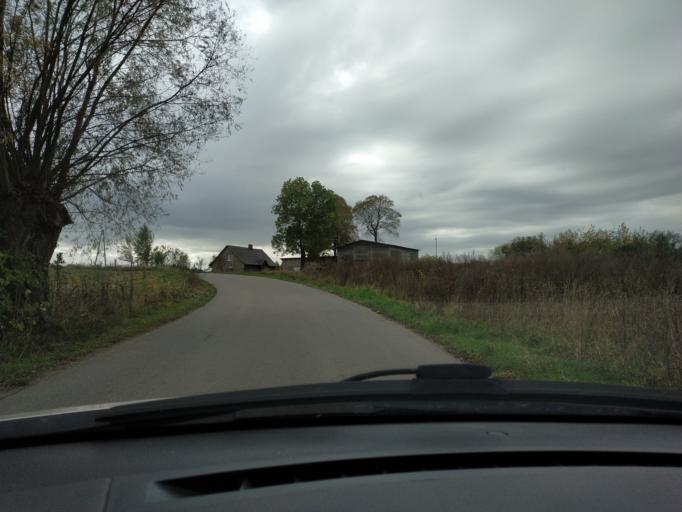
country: PL
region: Warmian-Masurian Voivodeship
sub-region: Powiat nowomiejski
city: Biskupiec
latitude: 53.4606
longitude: 19.3183
